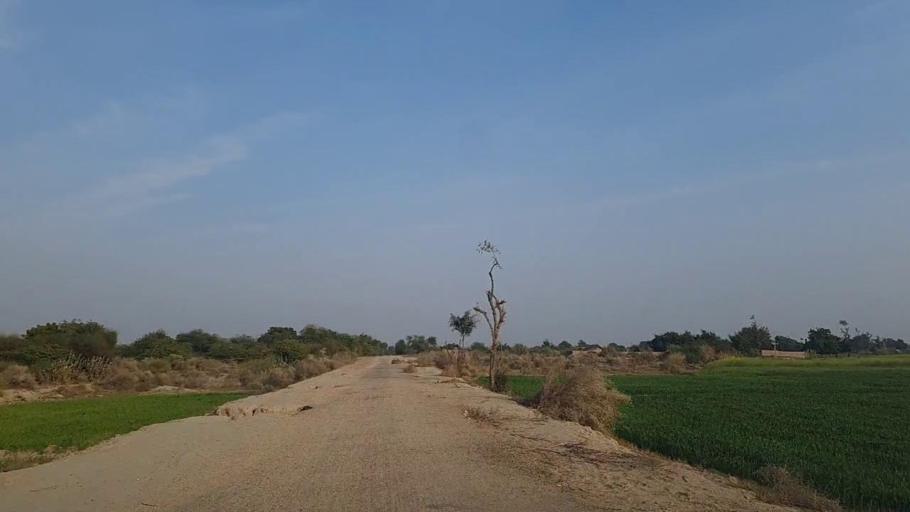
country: PK
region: Sindh
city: Jam Sahib
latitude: 26.4373
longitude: 68.5950
